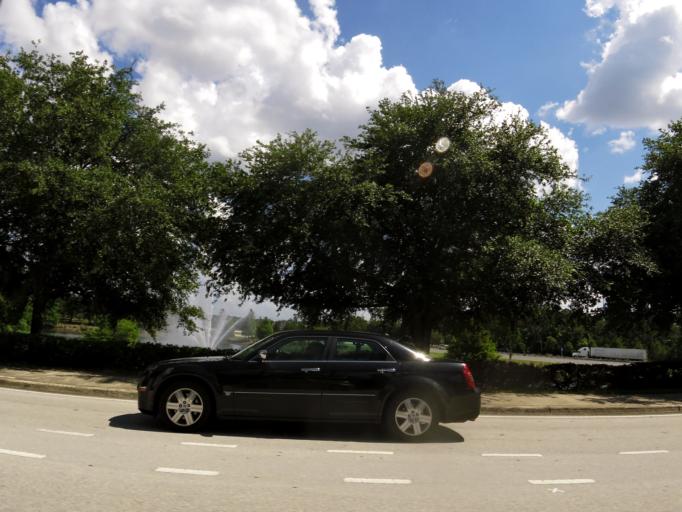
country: US
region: Florida
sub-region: Saint Johns County
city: Fruit Cove
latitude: 30.1412
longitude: -81.5385
